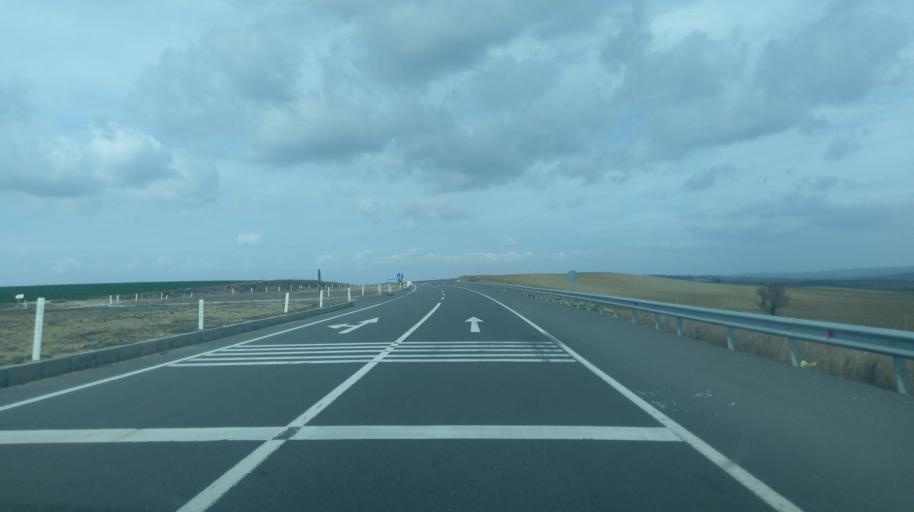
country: TR
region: Edirne
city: Hamidiye
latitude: 41.0260
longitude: 26.6352
